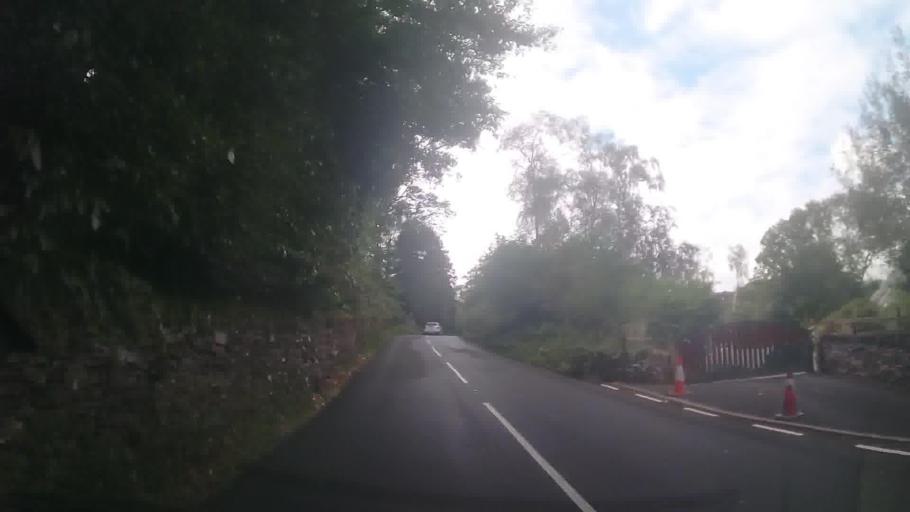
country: GB
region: England
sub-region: Cumbria
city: Ambleside
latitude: 54.4183
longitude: -3.0220
